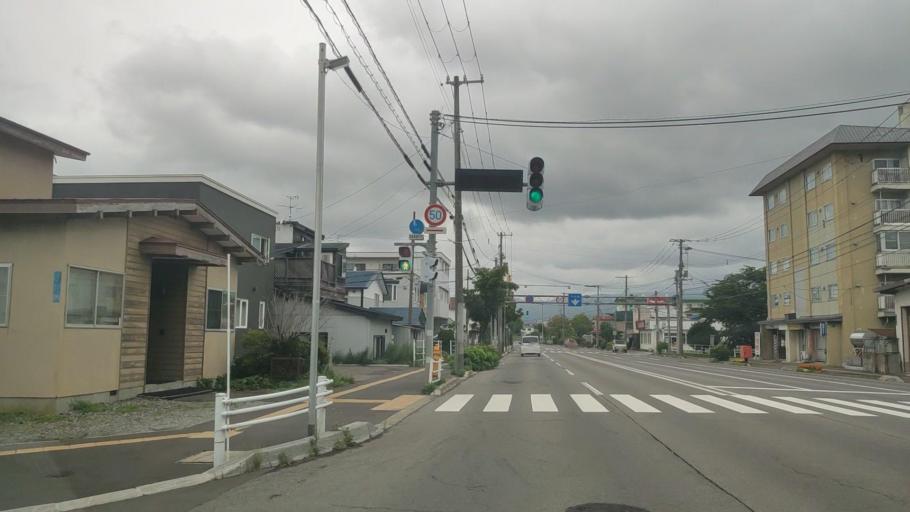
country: JP
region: Hokkaido
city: Hakodate
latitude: 41.7965
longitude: 140.7512
